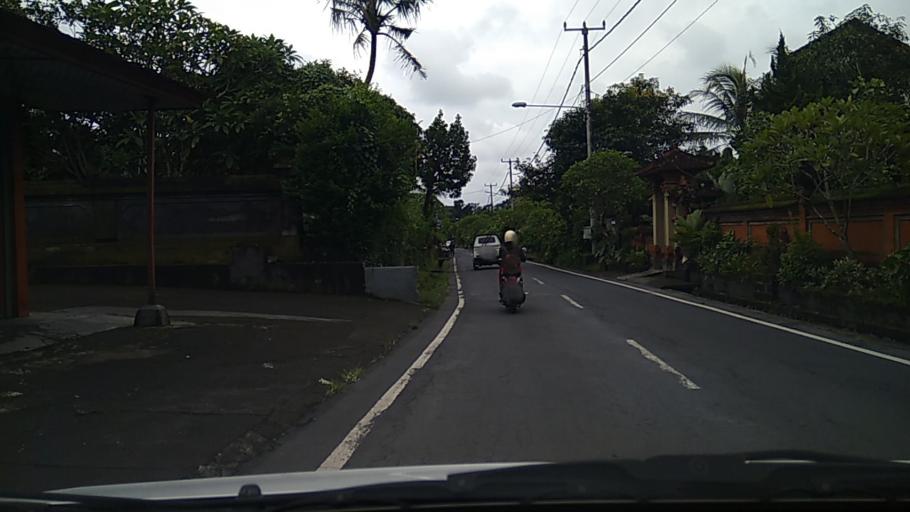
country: ID
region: Bali
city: Banjar Tebongkang
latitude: -8.5248
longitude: 115.2336
